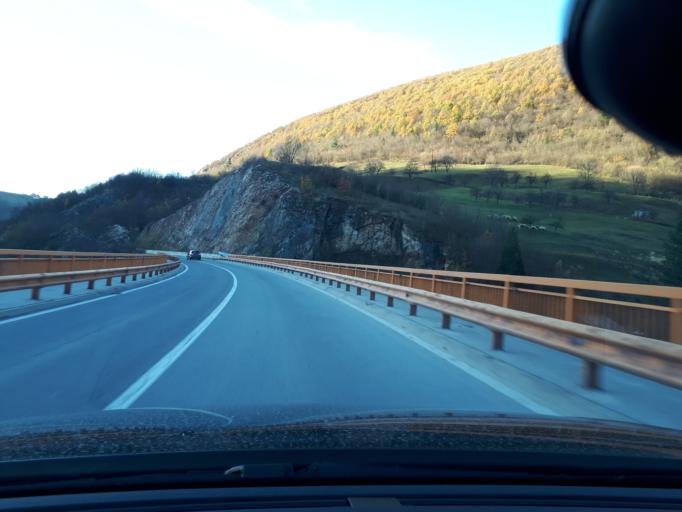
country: BA
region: Federation of Bosnia and Herzegovina
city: Kobilja Glava
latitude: 43.8526
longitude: 18.4637
